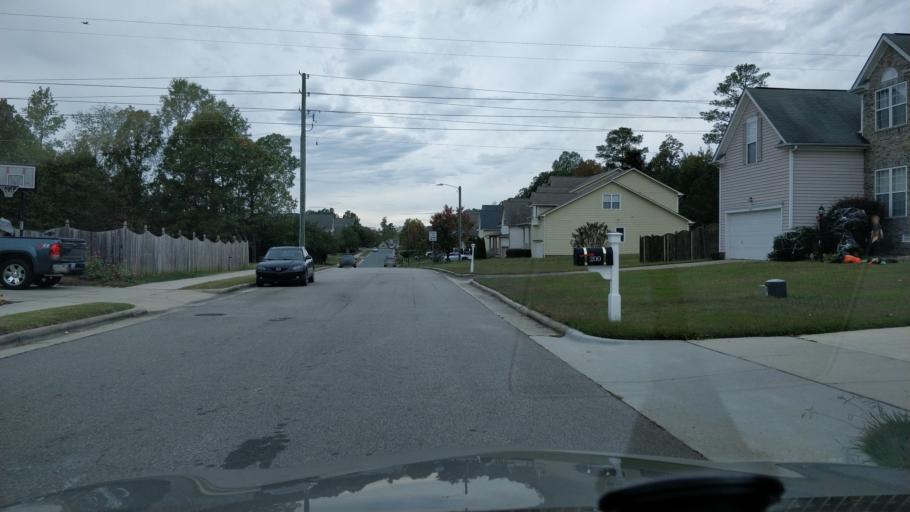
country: US
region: North Carolina
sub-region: Wake County
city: Morrisville
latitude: 35.8220
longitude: -78.8391
